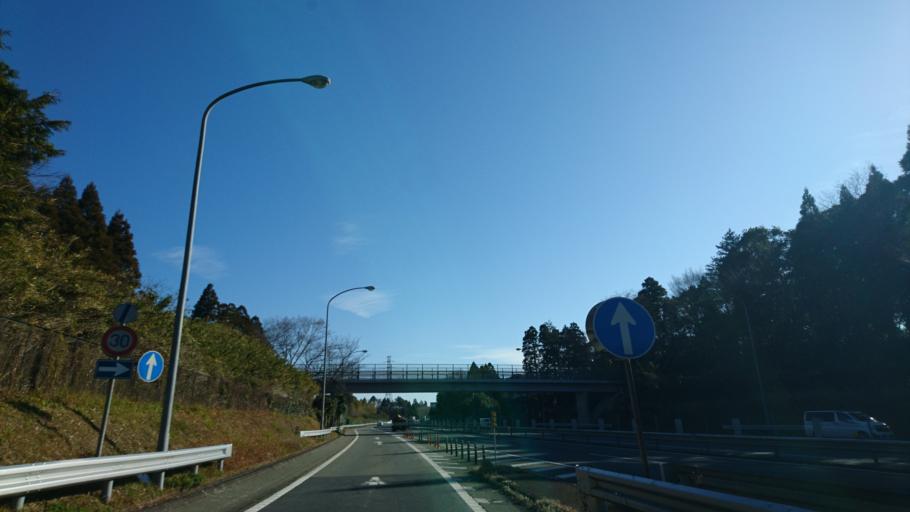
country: JP
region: Chiba
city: Oami
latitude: 35.5700
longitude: 140.2368
